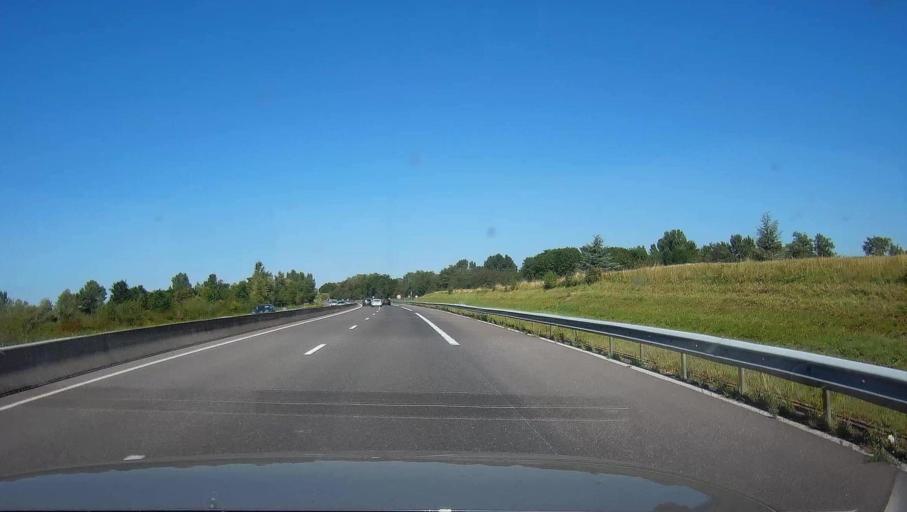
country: FR
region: Champagne-Ardenne
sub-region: Departement de la Marne
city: Fagnieres
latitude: 49.0070
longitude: 4.2987
